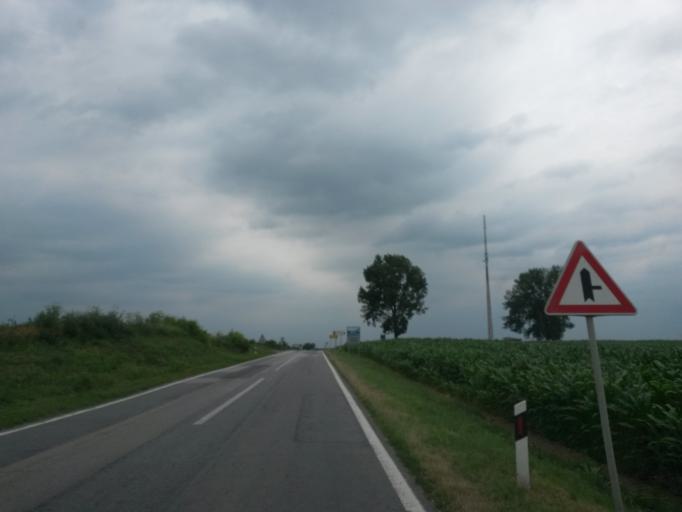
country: HR
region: Vukovarsko-Srijemska
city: Vukovar
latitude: 45.3195
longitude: 19.0679
